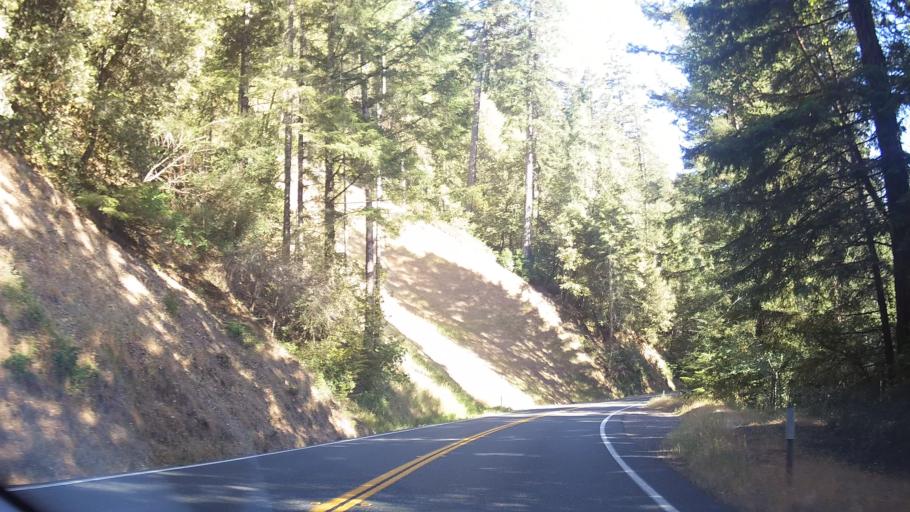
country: US
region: California
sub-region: Mendocino County
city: Brooktrails
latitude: 39.3579
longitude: -123.5093
